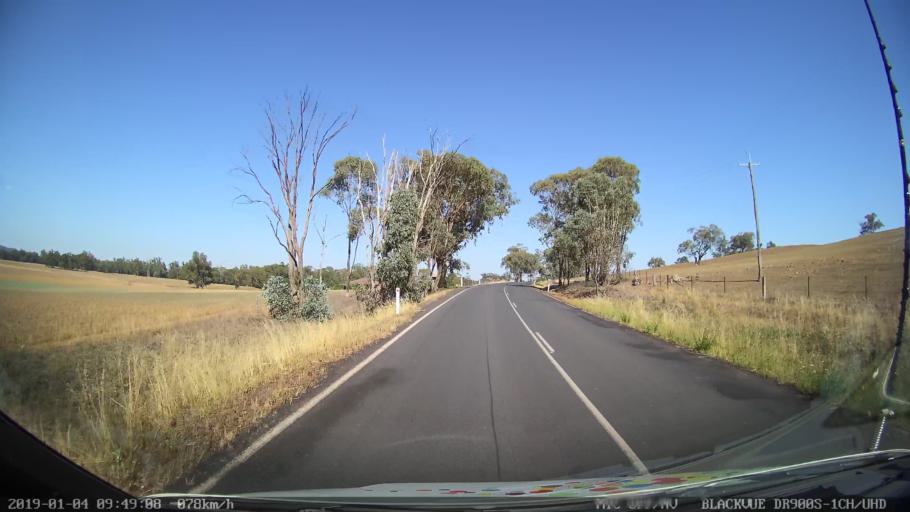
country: AU
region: New South Wales
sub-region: Cabonne
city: Canowindra
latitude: -33.5966
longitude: 148.4231
